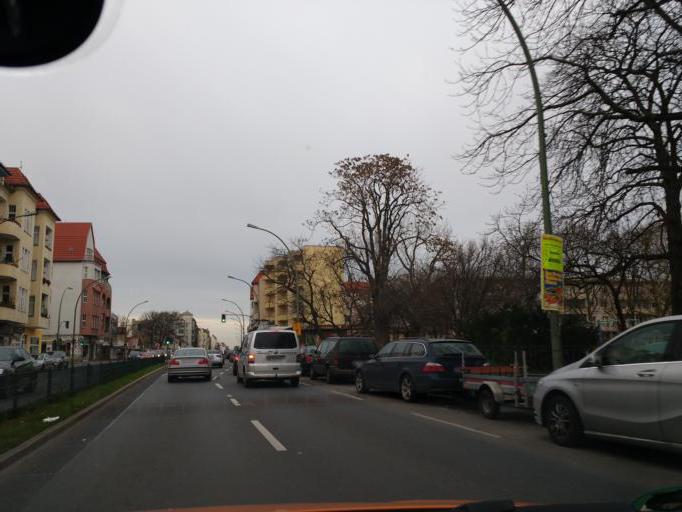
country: DE
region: Berlin
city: Mariendorf
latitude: 52.4426
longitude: 13.3865
